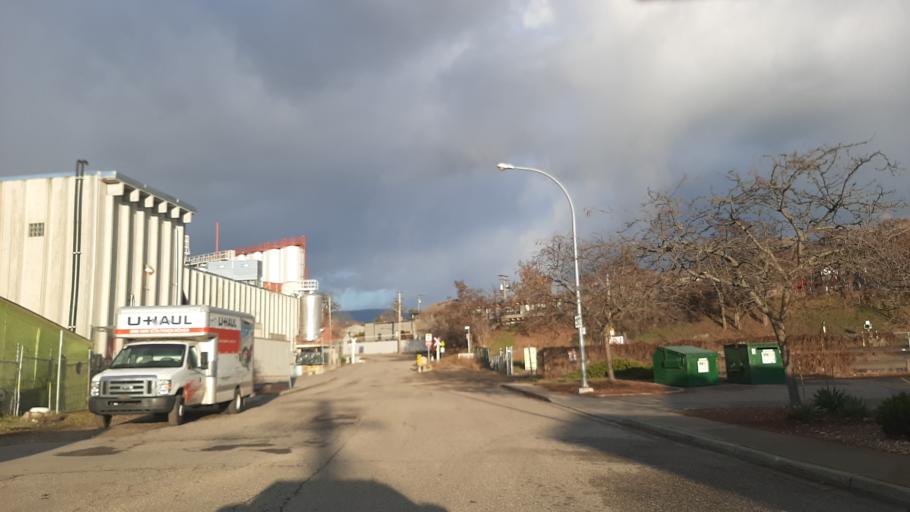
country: CA
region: British Columbia
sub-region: Regional District of North Okanagan
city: Vernon
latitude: 50.2610
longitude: -119.2693
